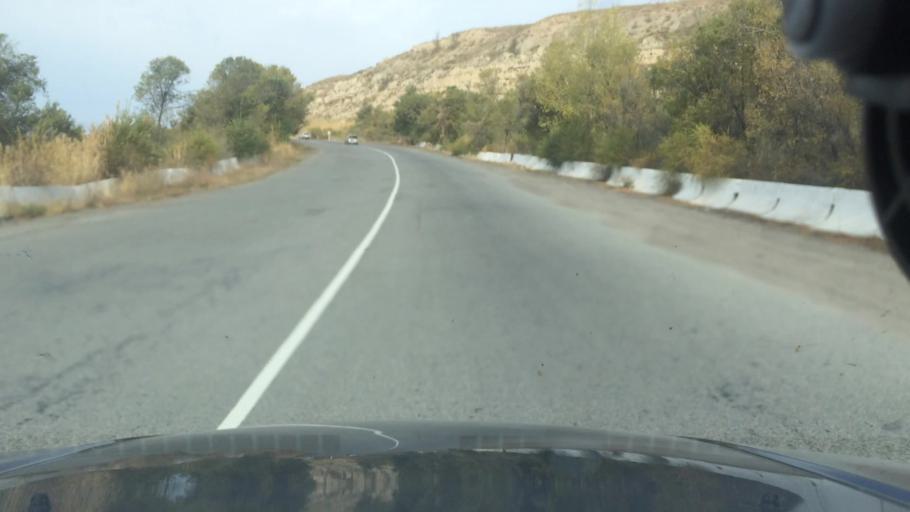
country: KG
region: Ysyk-Koel
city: Karakol
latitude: 42.5947
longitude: 78.3845
